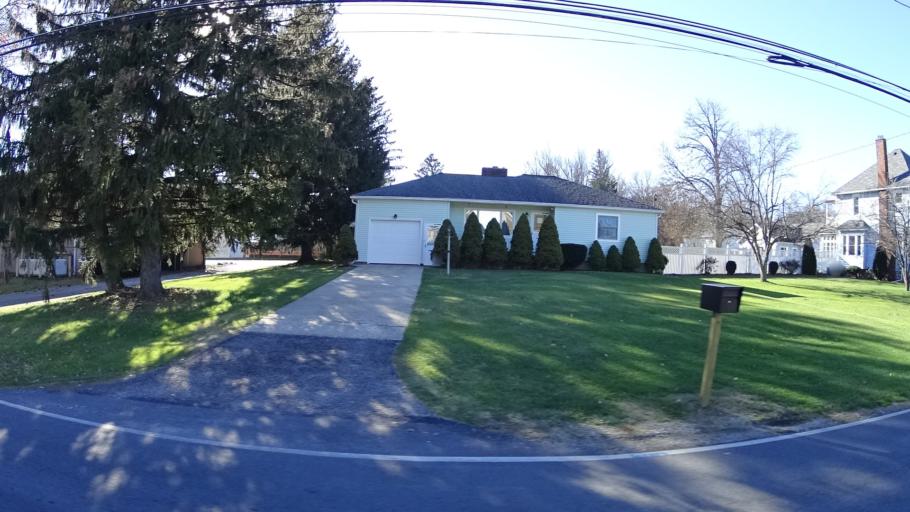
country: US
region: Ohio
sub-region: Lorain County
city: Elyria
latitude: 41.4002
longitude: -82.1328
